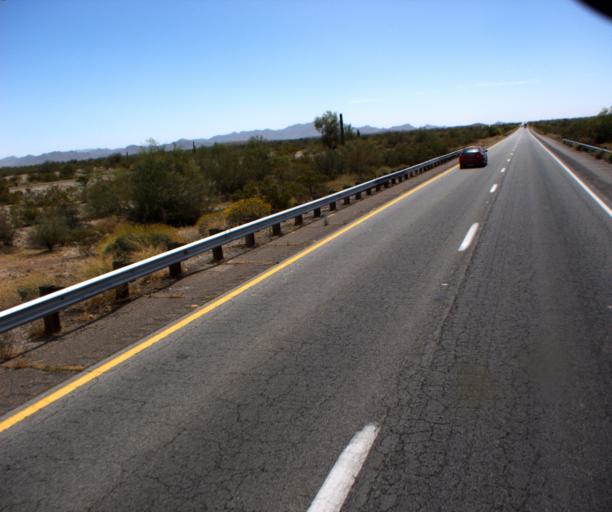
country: US
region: Arizona
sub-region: Maricopa County
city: Buckeye
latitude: 33.2867
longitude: -112.6302
